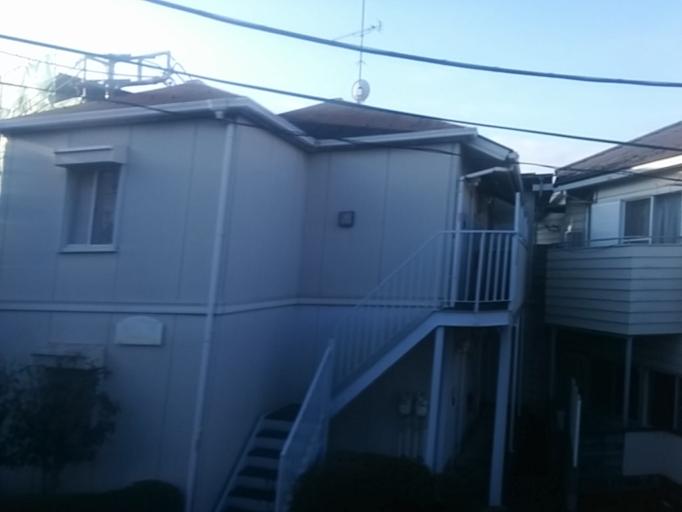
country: JP
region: Saitama
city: Wako
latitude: 35.7698
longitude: 139.6470
